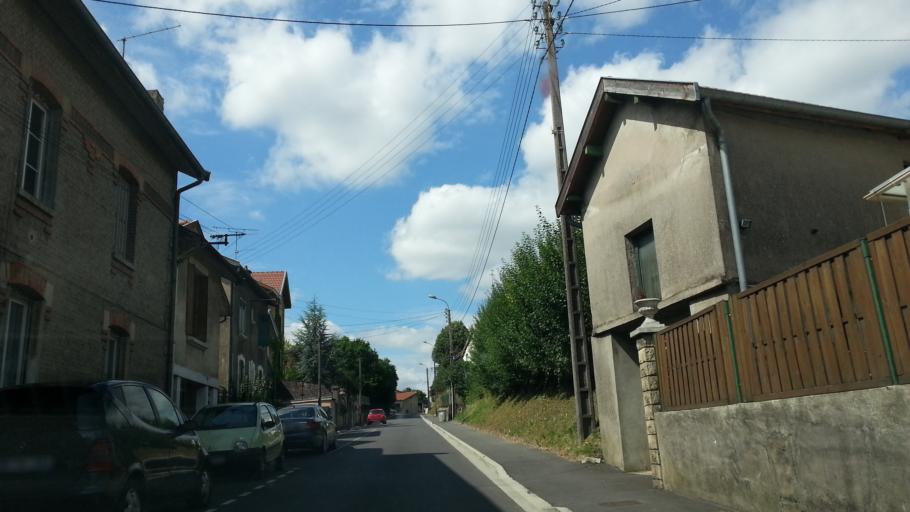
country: FR
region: Lorraine
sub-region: Departement de la Meuse
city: Thierville-sur-Meuse
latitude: 49.1591
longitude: 5.3639
